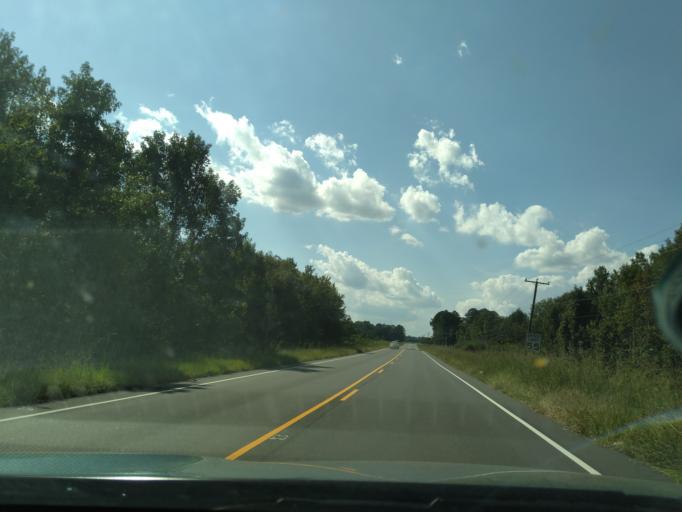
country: US
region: North Carolina
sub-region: Martin County
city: Robersonville
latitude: 35.8249
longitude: -77.2707
